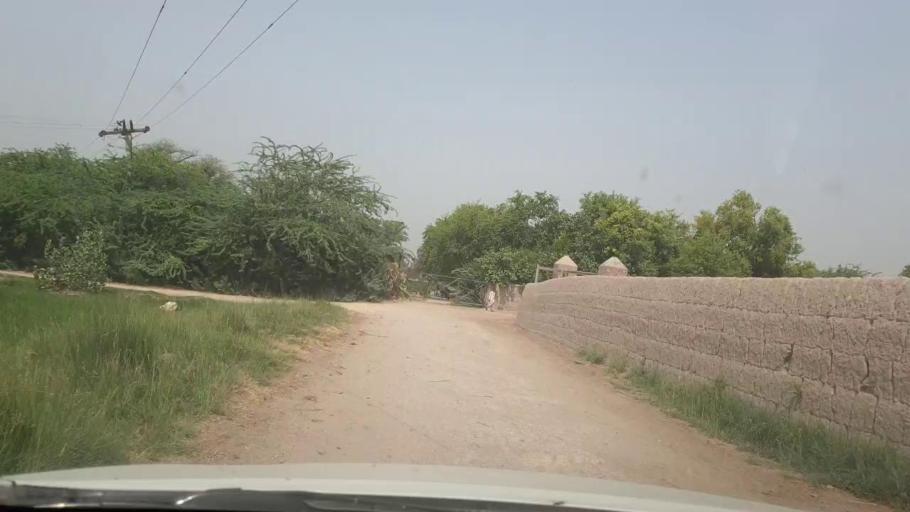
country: PK
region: Sindh
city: Kot Diji
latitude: 27.3062
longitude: 68.6853
